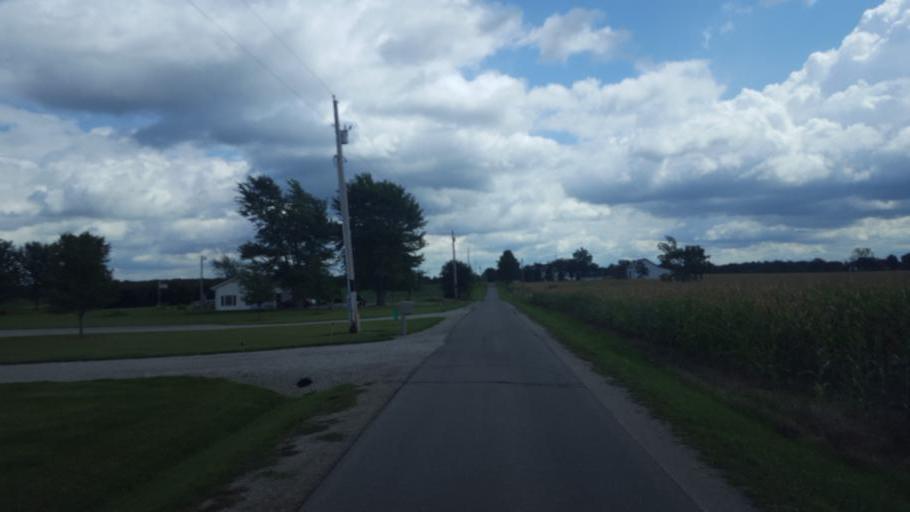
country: US
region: Ohio
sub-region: Huron County
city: Willard
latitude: 41.1152
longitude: -82.7640
